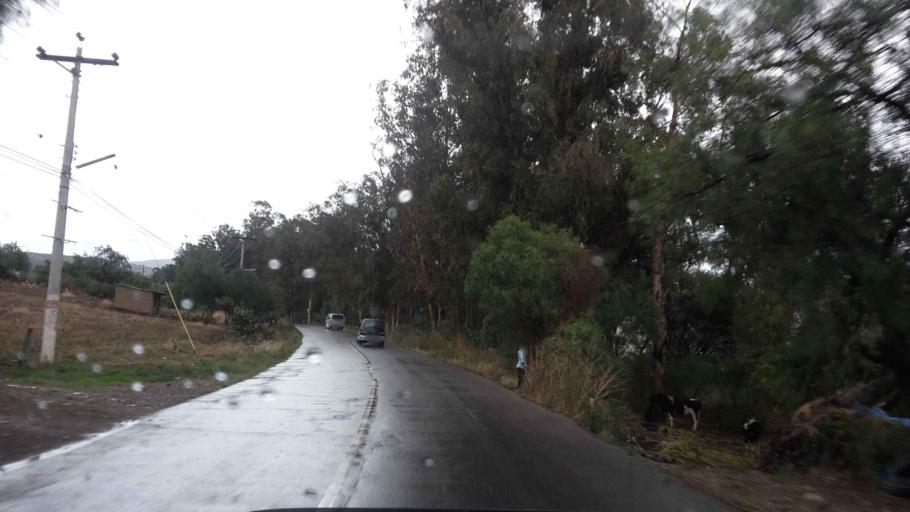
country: BO
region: Cochabamba
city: Tarata
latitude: -17.5406
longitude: -66.1084
